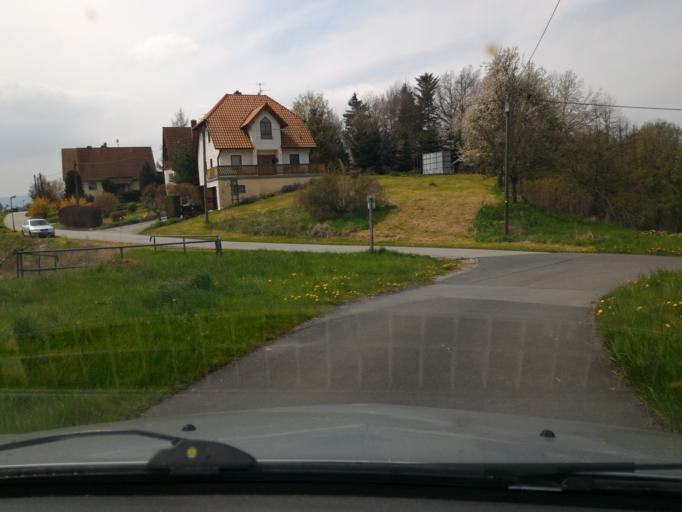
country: DE
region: Saxony
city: Hainewalde
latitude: 50.9176
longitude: 14.7180
